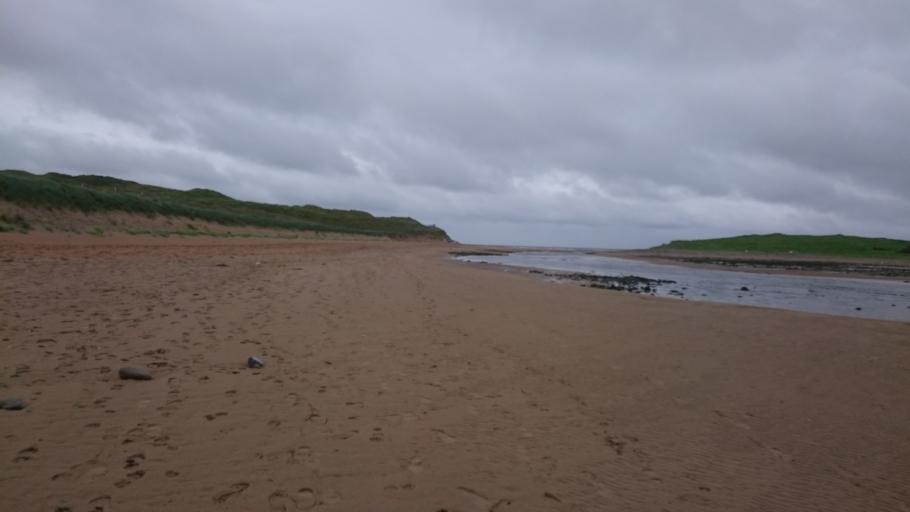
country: IE
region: Munster
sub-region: An Clar
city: Kilrush
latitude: 52.9451
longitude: -9.3547
